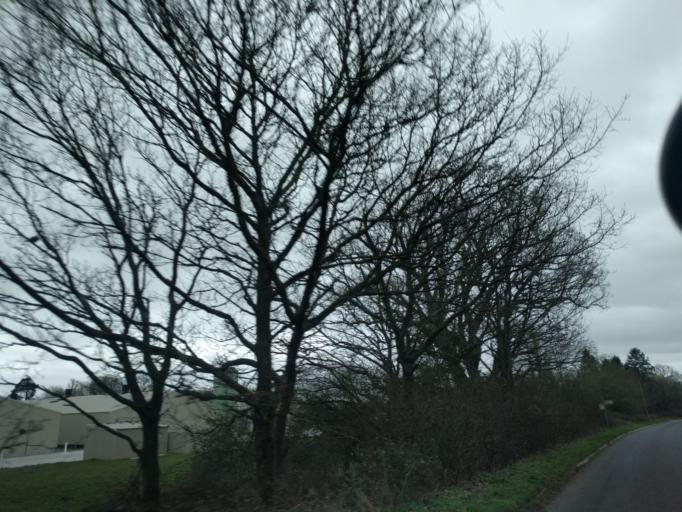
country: GB
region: England
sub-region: Wiltshire
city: Biddestone
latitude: 51.5091
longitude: -2.2001
